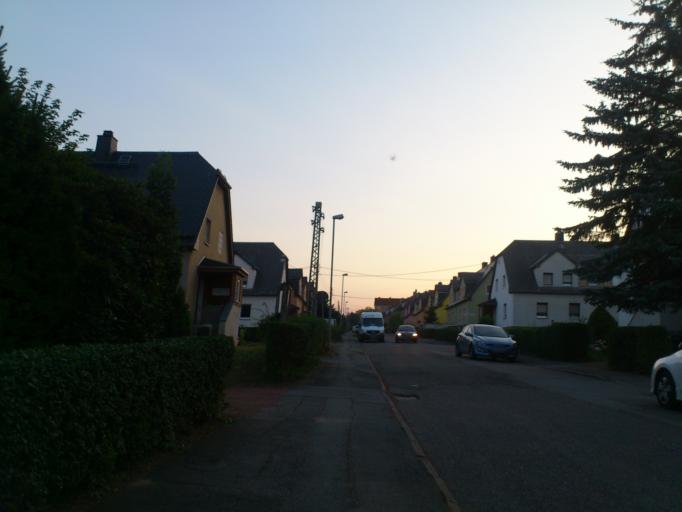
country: DE
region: Saxony
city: Neukirchen
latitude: 50.7762
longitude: 12.8657
